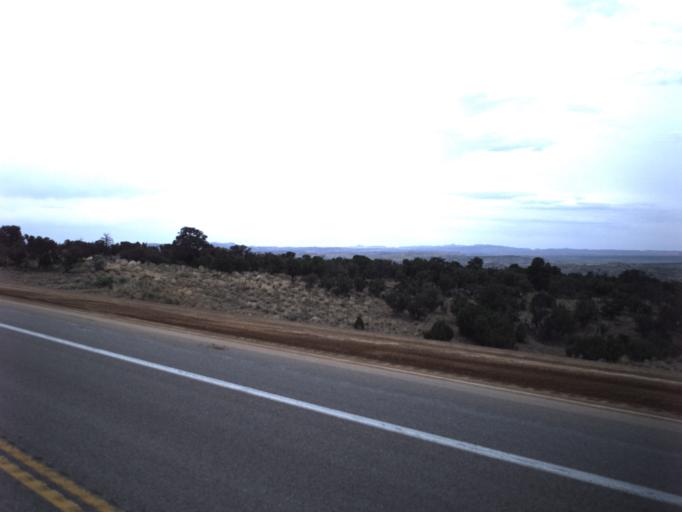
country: US
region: Utah
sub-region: Carbon County
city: East Carbon City
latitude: 39.4084
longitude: -110.4300
